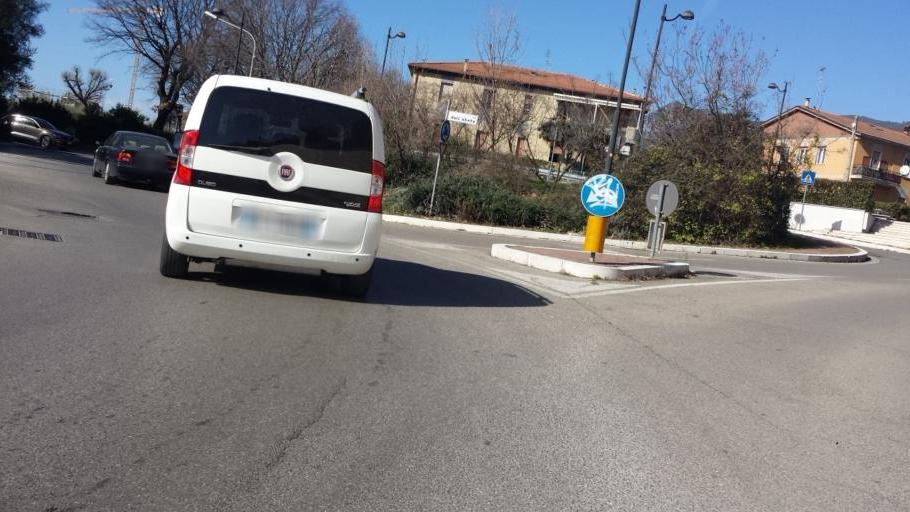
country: IT
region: Umbria
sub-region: Provincia di Terni
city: Terni
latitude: 42.5833
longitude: 12.6159
